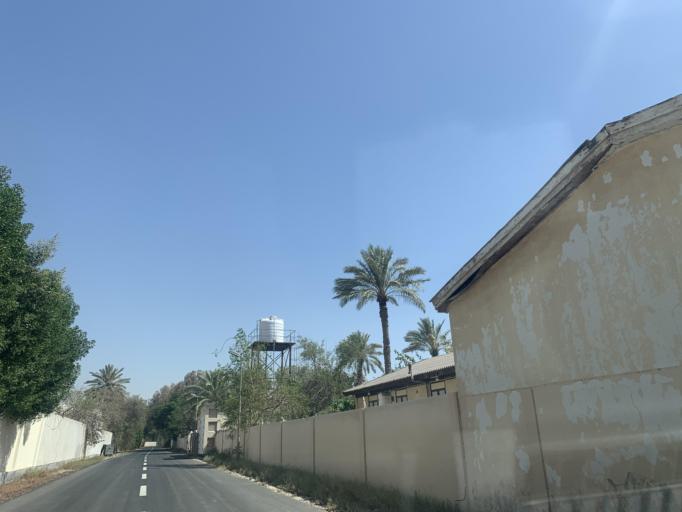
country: BH
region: Manama
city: Jidd Hafs
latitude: 26.2276
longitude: 50.5019
